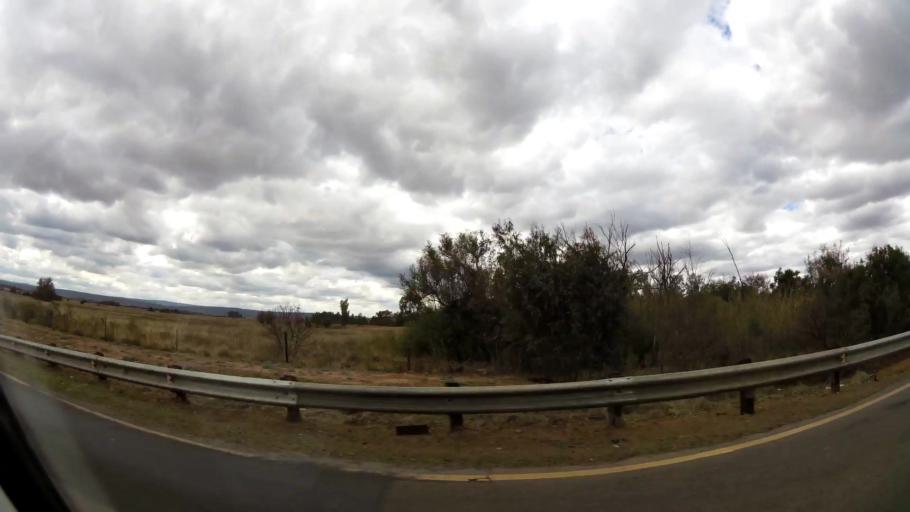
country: ZA
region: Limpopo
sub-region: Waterberg District Municipality
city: Modimolle
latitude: -24.7484
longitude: 28.4435
